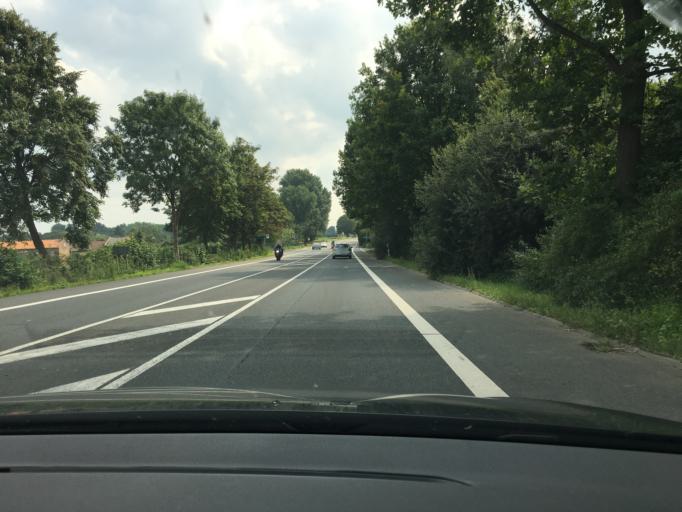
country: DE
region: North Rhine-Westphalia
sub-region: Regierungsbezirk Koln
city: Norvenich
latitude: 50.7992
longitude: 6.6356
